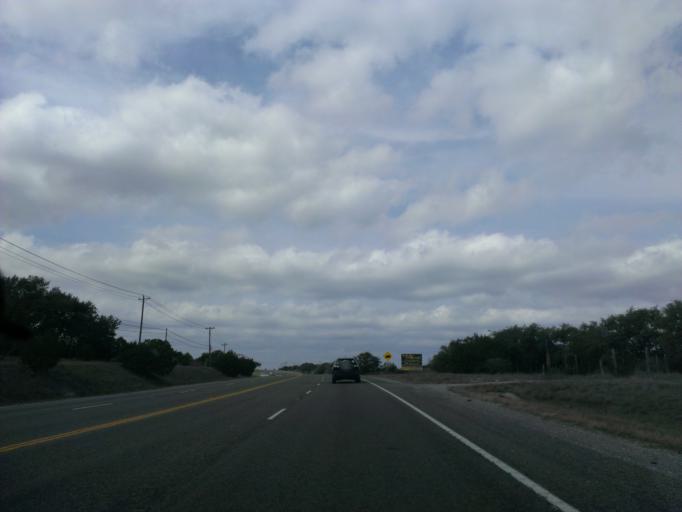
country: US
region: Texas
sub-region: Burnet County
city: Marble Falls
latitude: 30.4872
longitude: -98.2110
